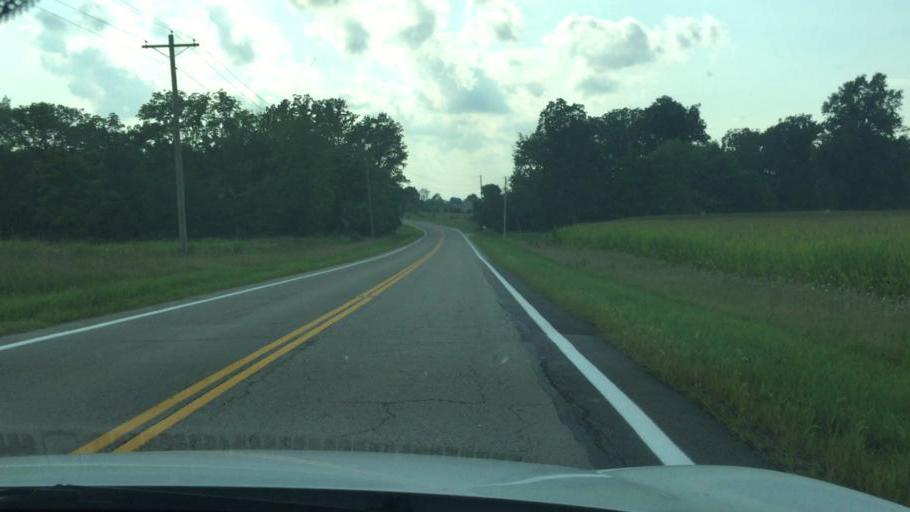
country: US
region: Ohio
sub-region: Champaign County
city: Mechanicsburg
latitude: 40.1004
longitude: -83.5599
